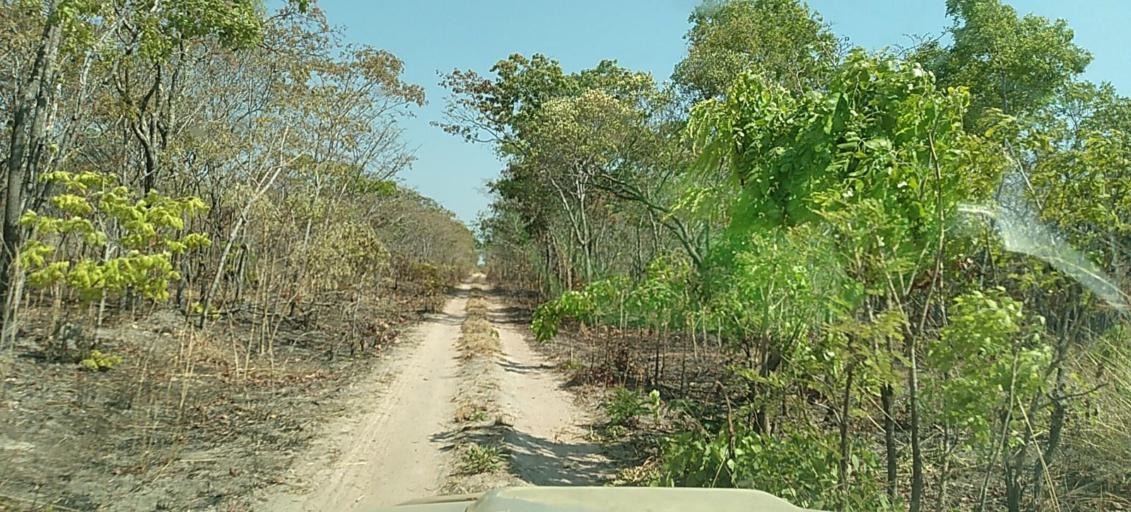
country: ZM
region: North-Western
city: Kalengwa
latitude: -13.3231
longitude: 24.8247
